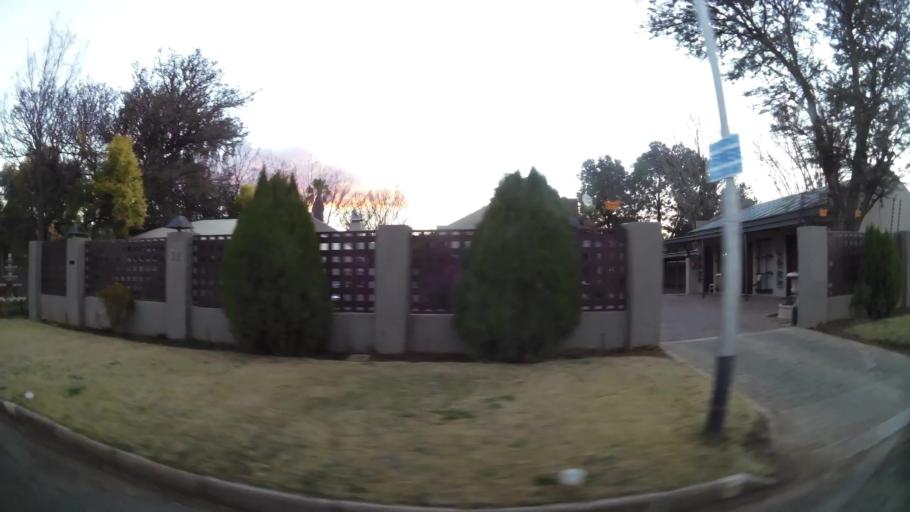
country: ZA
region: North-West
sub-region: Dr Kenneth Kaunda District Municipality
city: Potchefstroom
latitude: -26.7106
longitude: 27.1162
